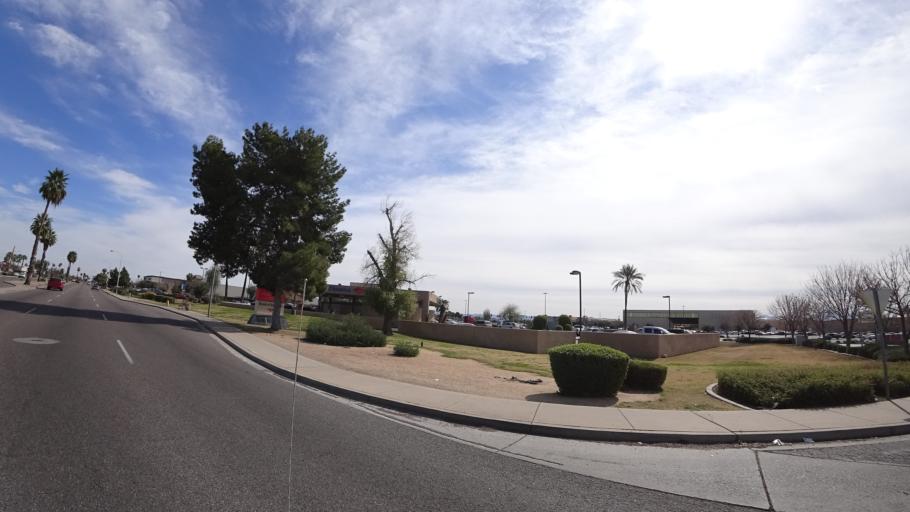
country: US
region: Arizona
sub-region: Maricopa County
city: Tolleson
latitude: 33.4800
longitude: -112.2247
